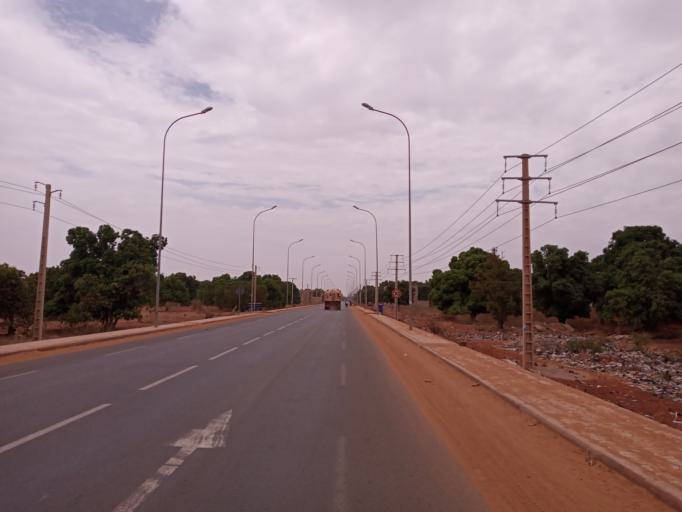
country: ML
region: Koulikoro
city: Koulikoro
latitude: 12.8487
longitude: -7.5754
